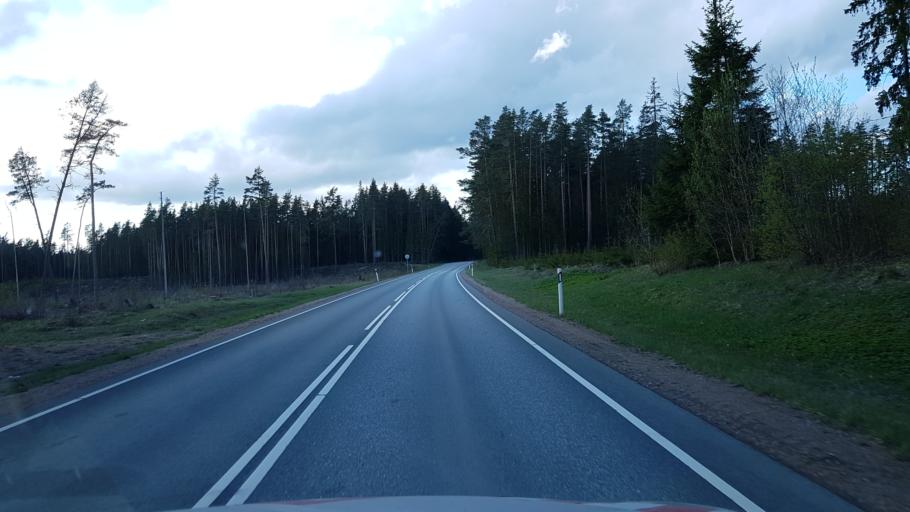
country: EE
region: Laeaene-Virumaa
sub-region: Tapa vald
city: Tapa
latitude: 59.4171
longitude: 25.9947
